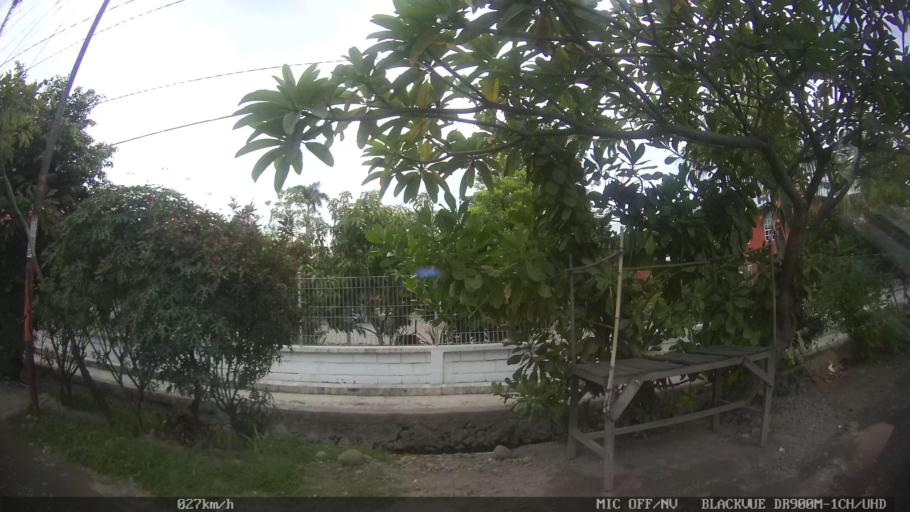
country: ID
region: North Sumatra
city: Labuhan Deli
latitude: 3.6736
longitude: 98.6757
